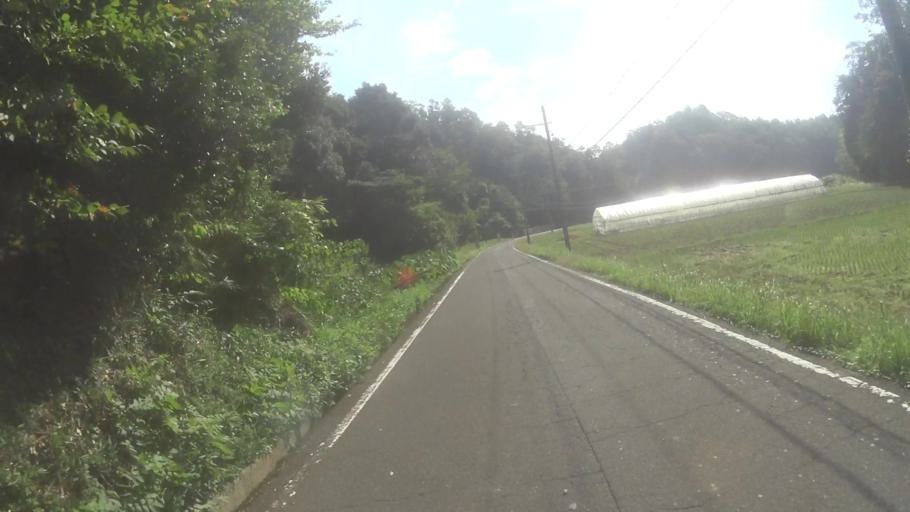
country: JP
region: Kyoto
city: Miyazu
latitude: 35.6828
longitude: 135.1108
